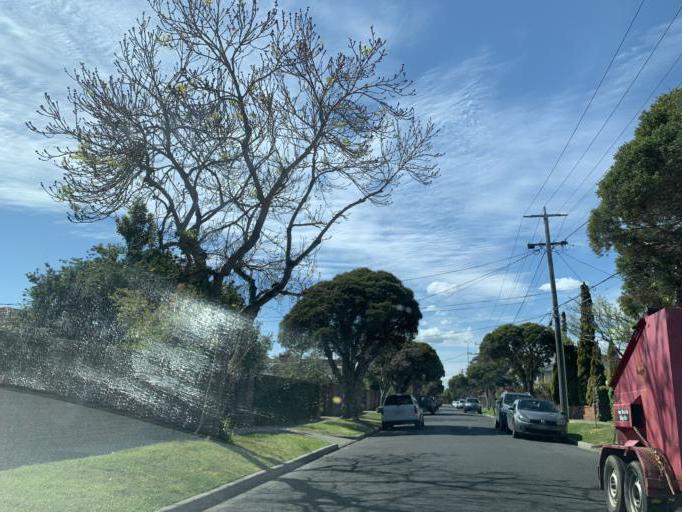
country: AU
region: Victoria
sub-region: Bayside
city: Hampton East
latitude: -37.9487
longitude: 145.0246
